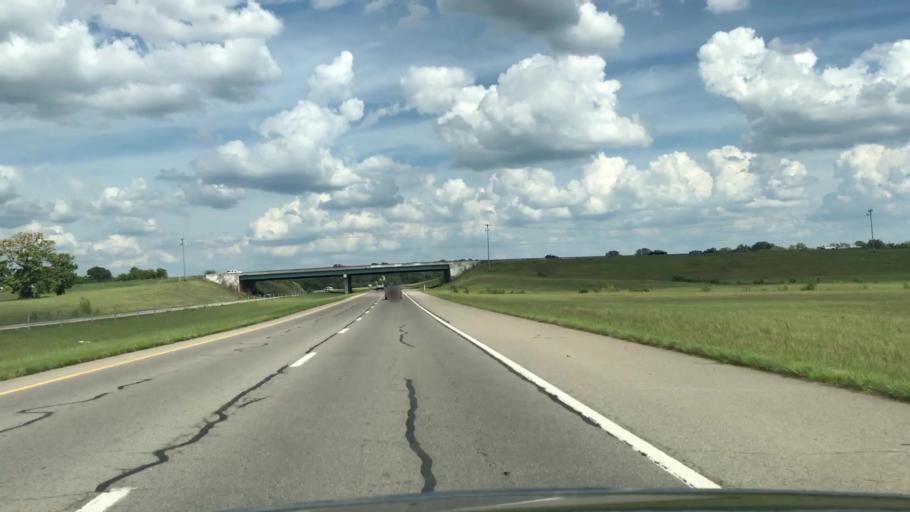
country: US
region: Tennessee
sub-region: Maury County
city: Spring Hill
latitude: 35.7343
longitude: -86.8972
